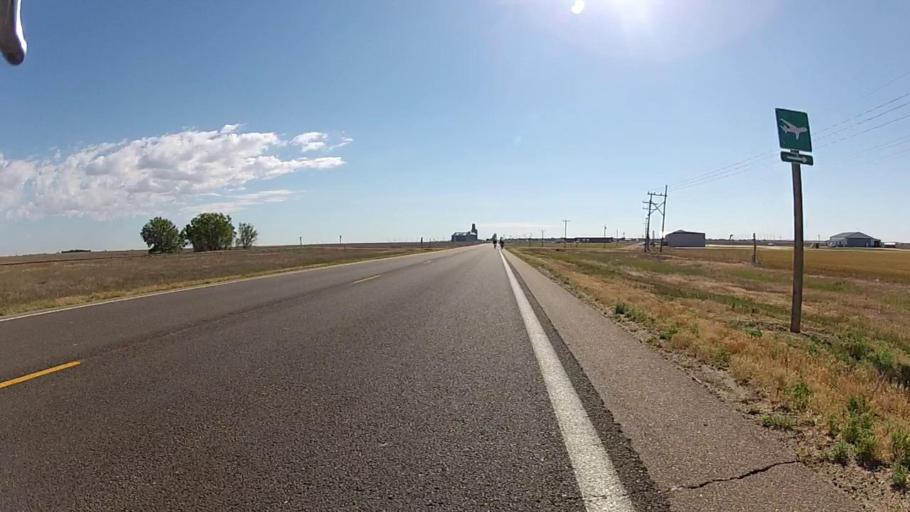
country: US
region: Kansas
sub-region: Gray County
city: Cimarron
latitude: 37.5913
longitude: -100.4714
